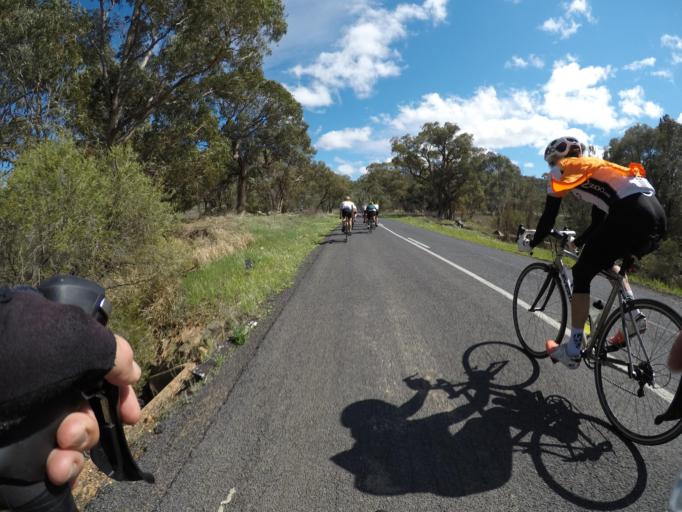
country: AU
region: New South Wales
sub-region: Parkes
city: Peak Hill
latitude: -32.6650
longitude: 148.5596
